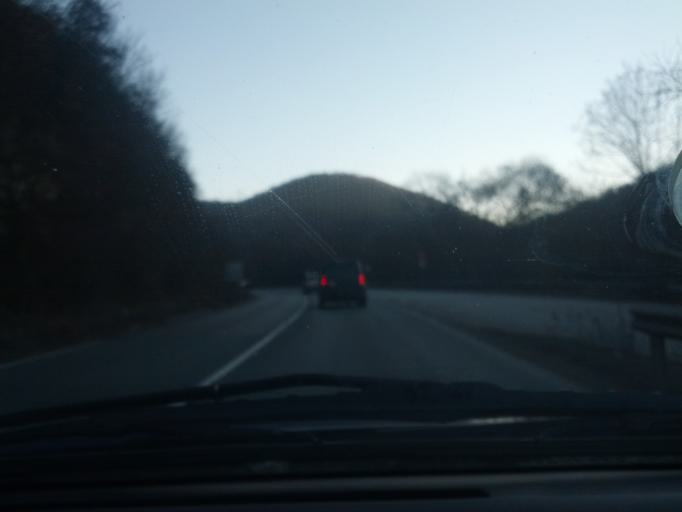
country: BG
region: Vratsa
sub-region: Obshtina Mezdra
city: Mezdra
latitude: 43.1089
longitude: 23.6796
